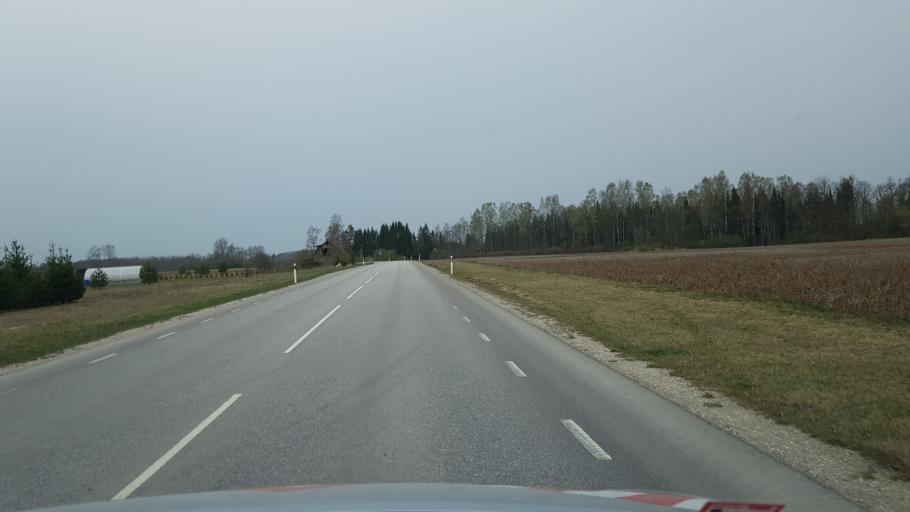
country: EE
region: Harju
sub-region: Raasiku vald
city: Arukula
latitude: 59.3805
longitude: 25.0066
